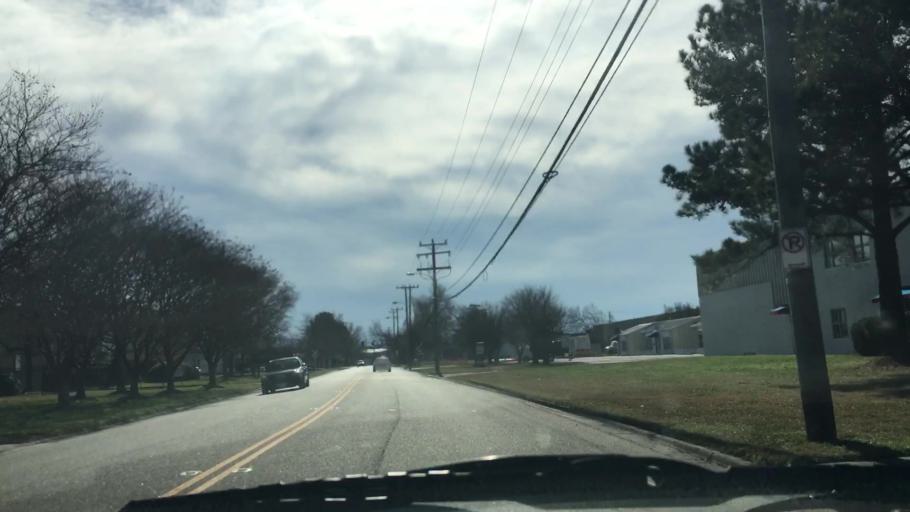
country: US
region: Virginia
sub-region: City of Norfolk
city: Norfolk
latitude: 36.8638
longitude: -76.2352
